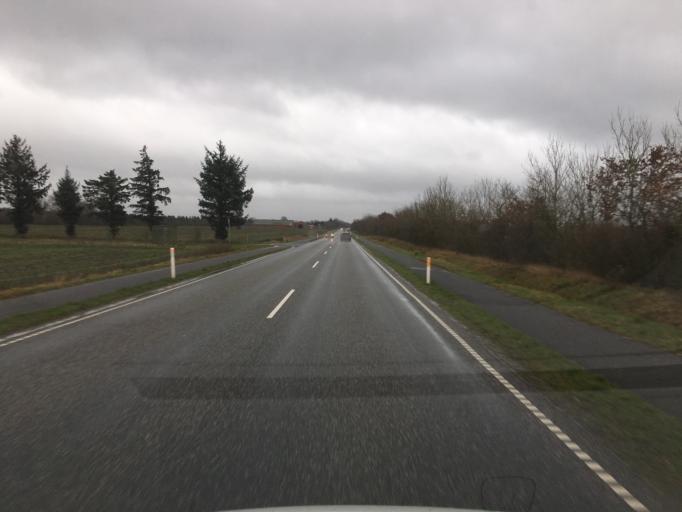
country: DK
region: South Denmark
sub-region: Aabenraa Kommune
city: Tinglev
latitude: 54.9139
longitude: 9.2516
